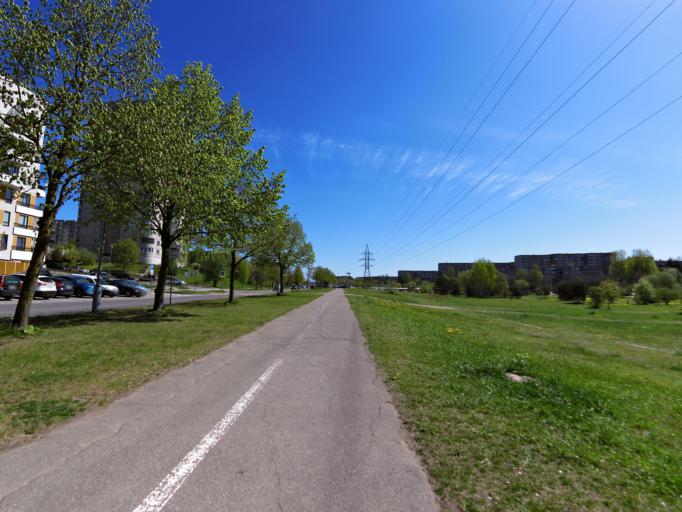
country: LT
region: Vilnius County
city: Seskine
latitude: 54.7200
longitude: 25.2509
